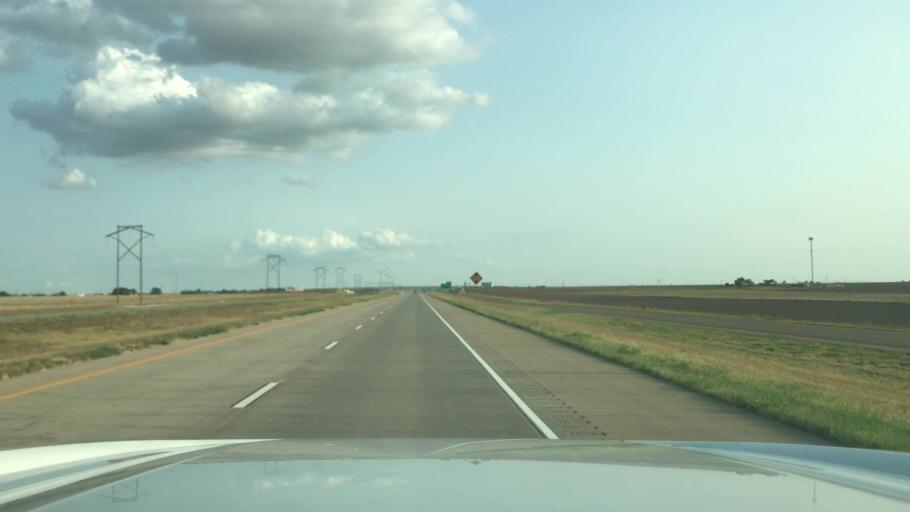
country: US
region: Texas
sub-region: Swisher County
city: Tulia
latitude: 34.5523
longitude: -101.7950
